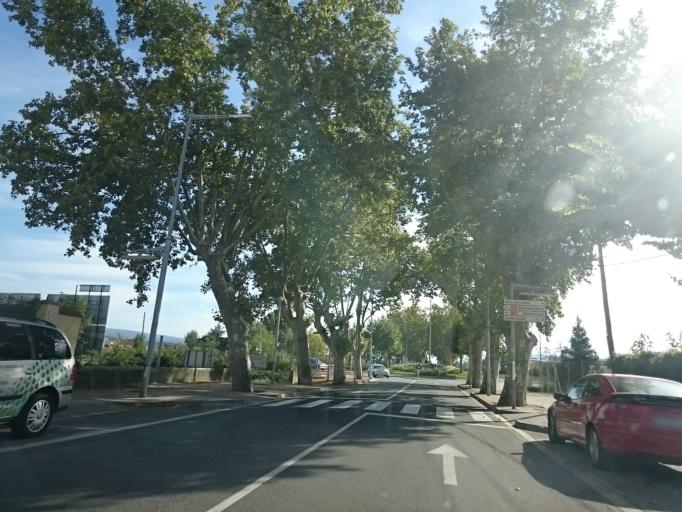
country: ES
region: Catalonia
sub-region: Provincia de Barcelona
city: Vic
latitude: 41.9191
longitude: 2.2521
